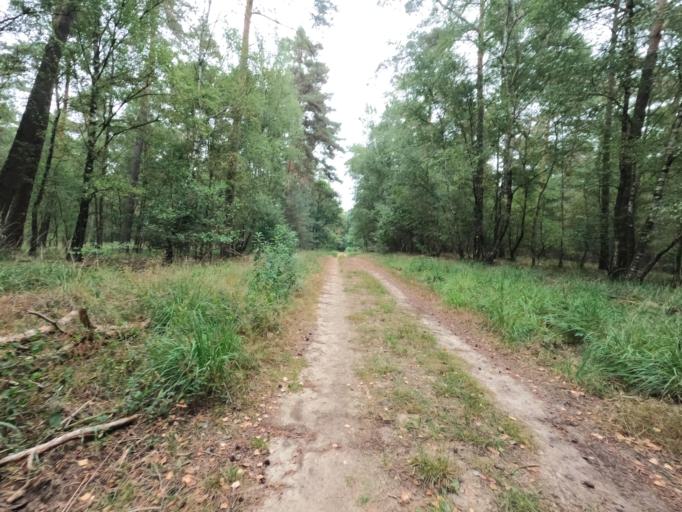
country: DE
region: North Rhine-Westphalia
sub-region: Regierungsbezirk Koln
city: Wassenberg
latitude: 51.1649
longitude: 6.1545
